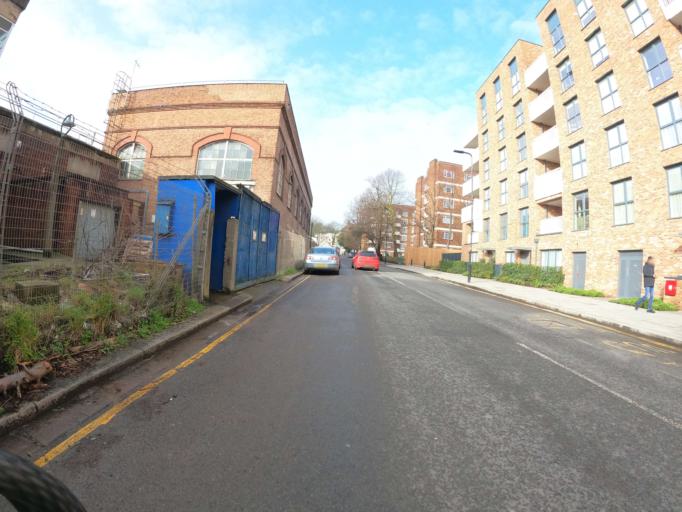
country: GB
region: England
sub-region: Greater London
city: Acton
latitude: 51.5023
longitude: -0.2789
